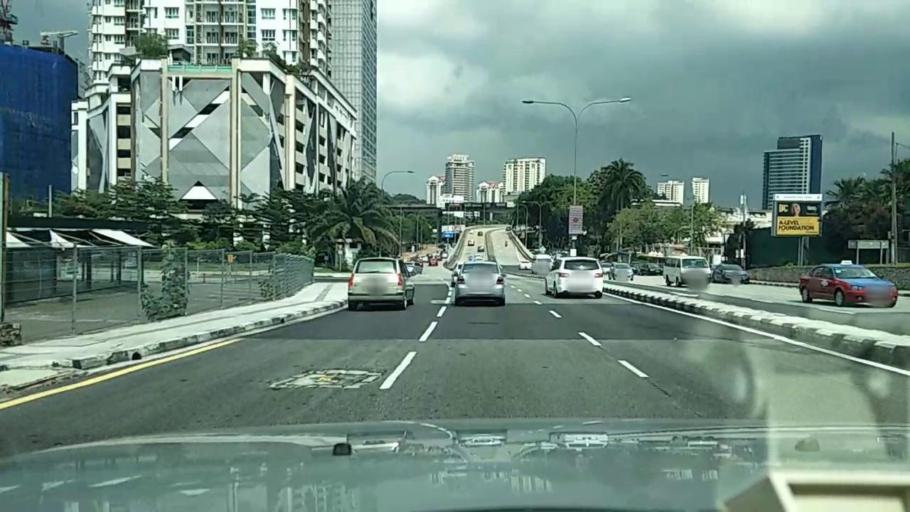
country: MY
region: Kuala Lumpur
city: Kuala Lumpur
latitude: 3.1275
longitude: 101.6755
